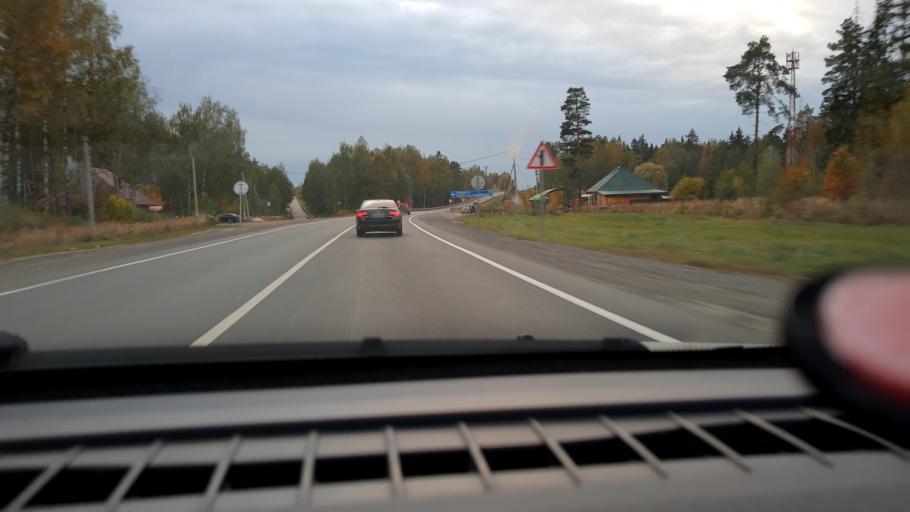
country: RU
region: Vladimir
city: Kameshkovo
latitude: 56.1933
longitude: 40.9307
